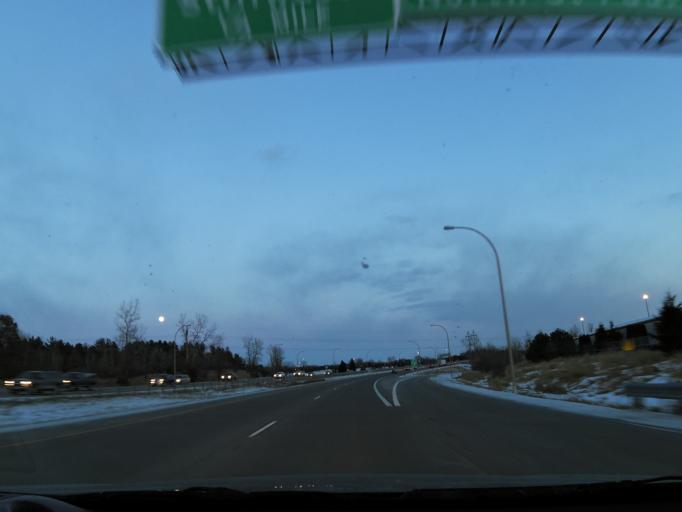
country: US
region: Minnesota
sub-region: Washington County
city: Birchwood
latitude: 45.0323
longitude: -92.9675
